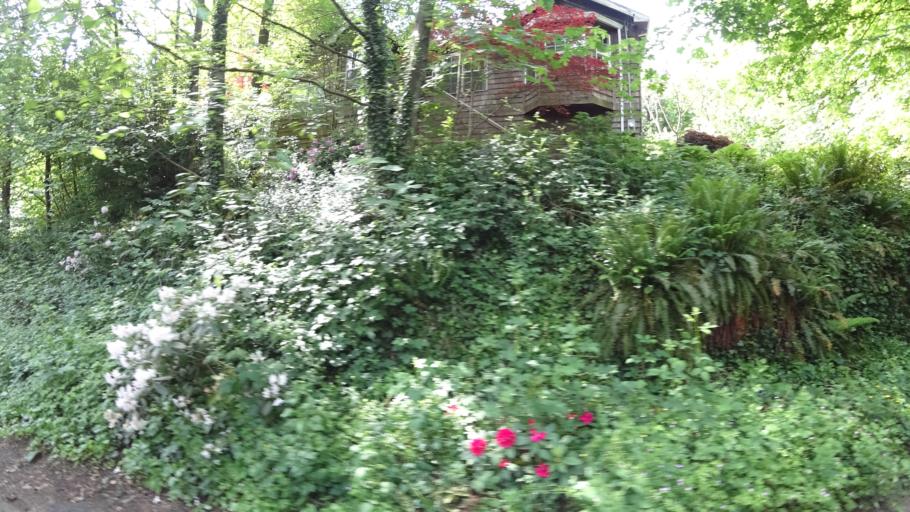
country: US
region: Oregon
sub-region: Multnomah County
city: Portland
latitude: 45.5065
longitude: -122.7098
